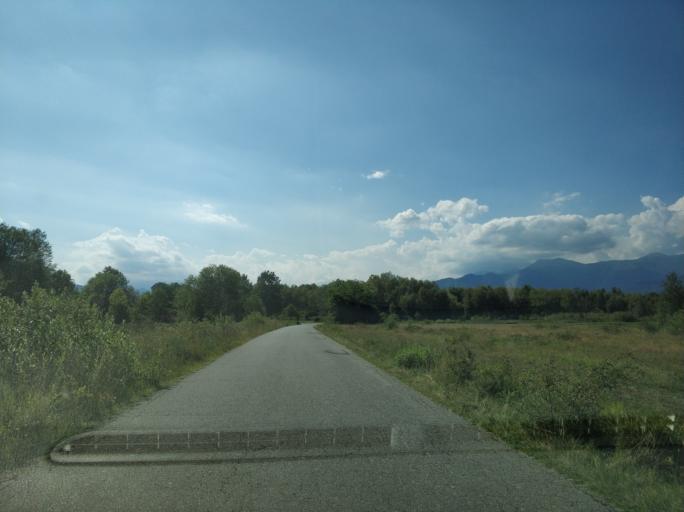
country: IT
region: Piedmont
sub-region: Provincia di Torino
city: San Carlo Canavese
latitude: 45.2579
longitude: 7.6172
